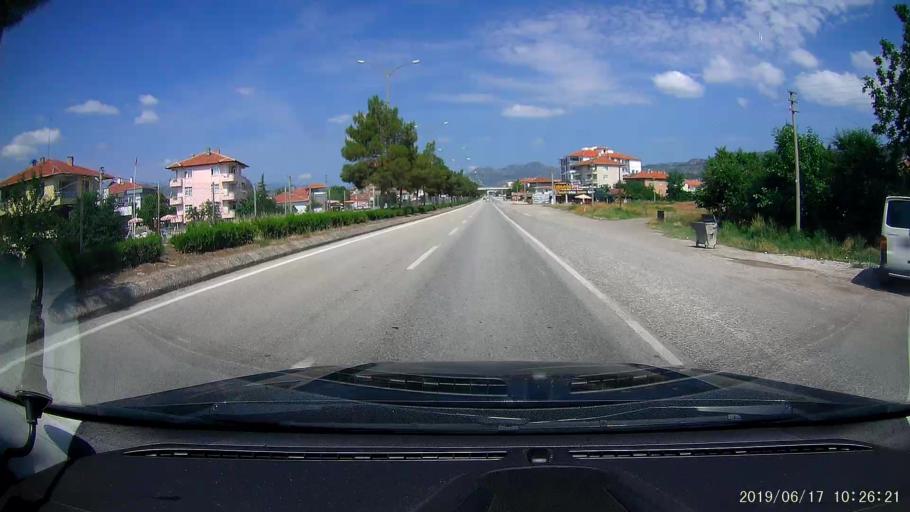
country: TR
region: Corum
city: Osmancik
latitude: 40.9730
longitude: 34.8202
